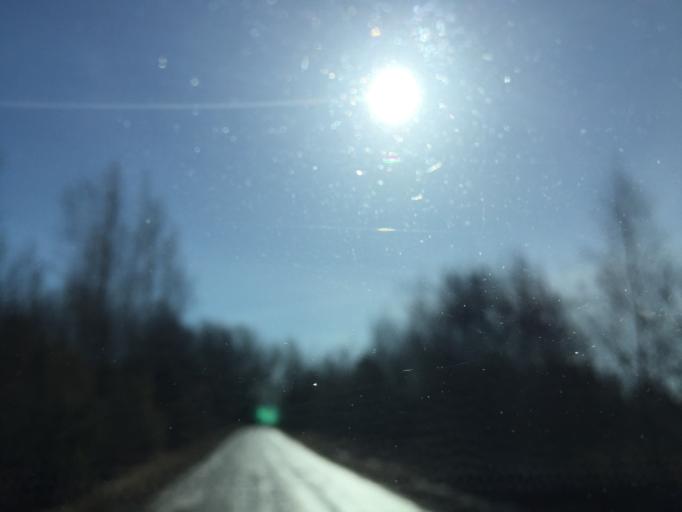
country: EE
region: Laeaene
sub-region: Haapsalu linn
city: Haapsalu
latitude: 58.6840
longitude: 23.5114
